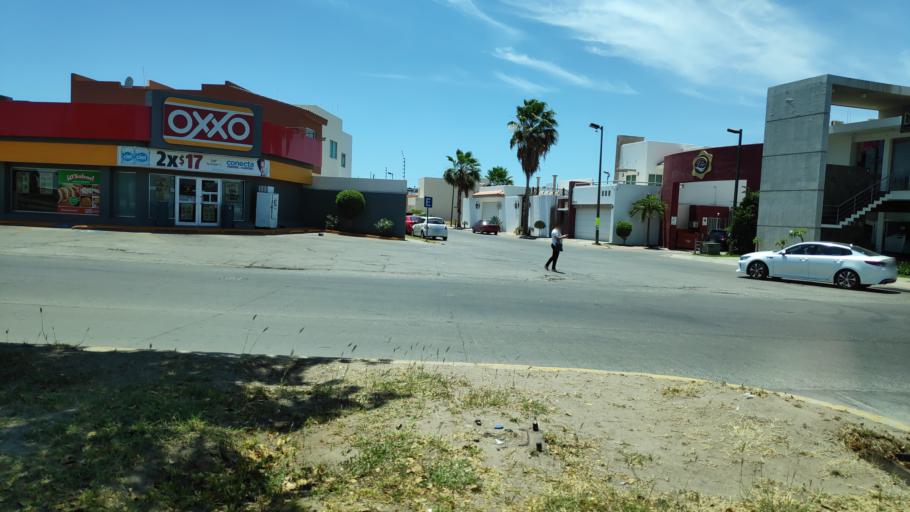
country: MX
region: Sinaloa
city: Culiacan
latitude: 24.8315
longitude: -107.3990
